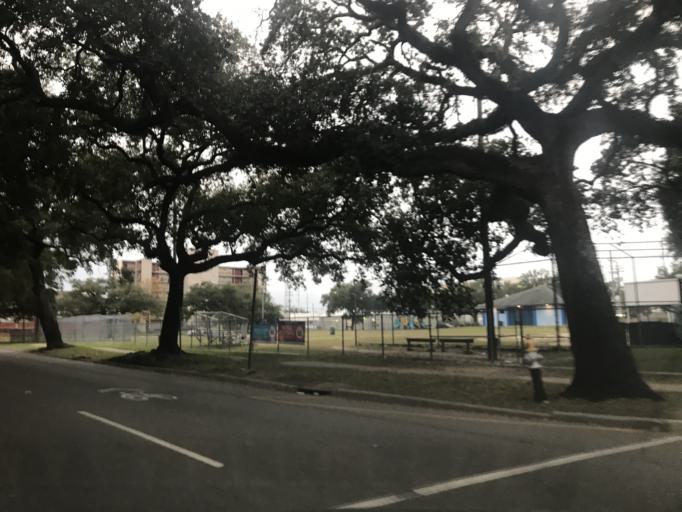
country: US
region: Louisiana
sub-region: Orleans Parish
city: New Orleans
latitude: 29.9667
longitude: -90.0974
